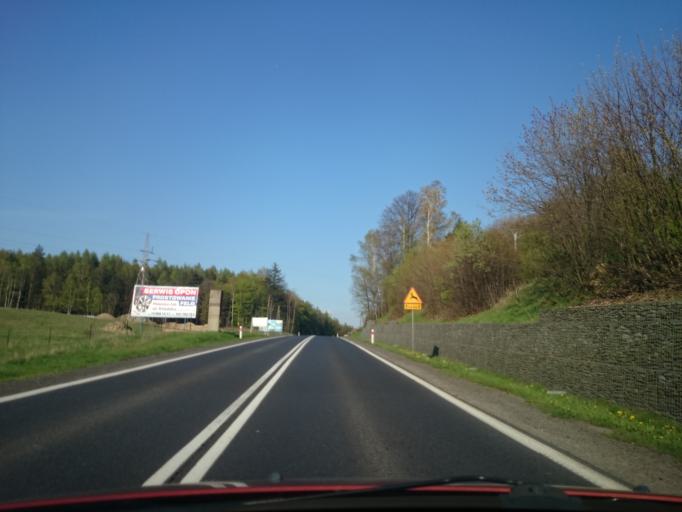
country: PL
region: Lower Silesian Voivodeship
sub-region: Powiat klodzki
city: Szczytna
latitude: 50.4233
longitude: 16.4605
